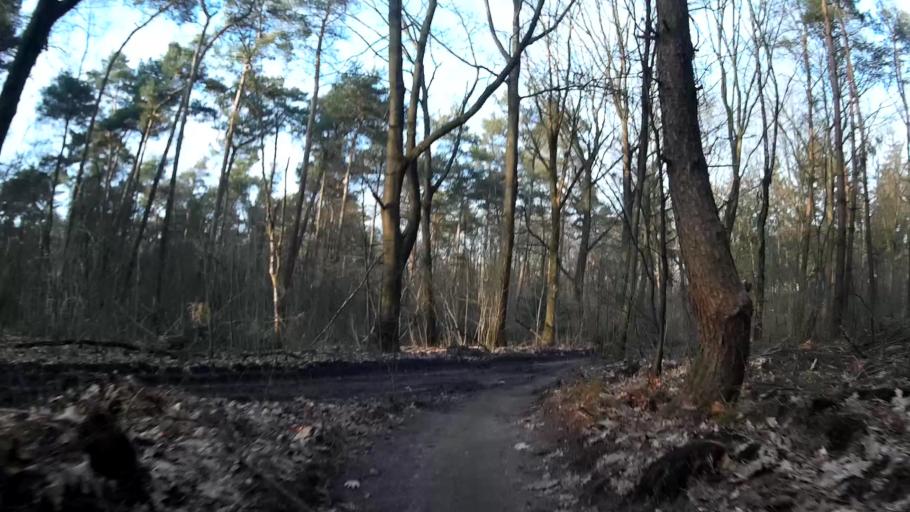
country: NL
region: Utrecht
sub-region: Gemeente Rhenen
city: Rhenen
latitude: 51.9718
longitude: 5.5567
